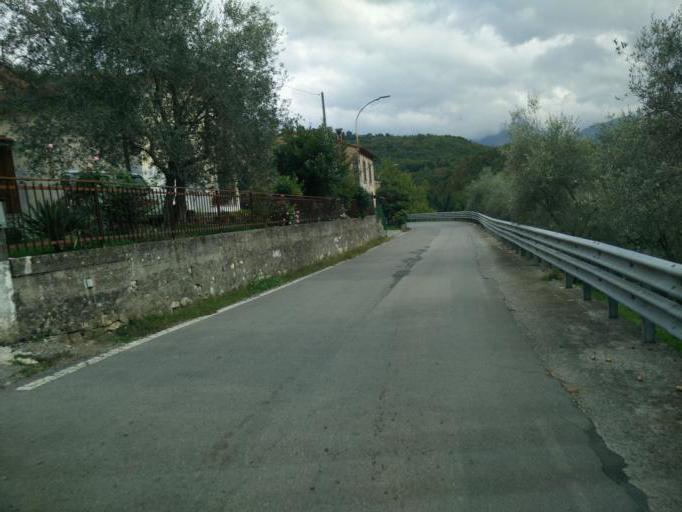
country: IT
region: Tuscany
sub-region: Provincia di Massa-Carrara
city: Casola in Lunigiana
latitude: 44.2148
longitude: 10.1886
